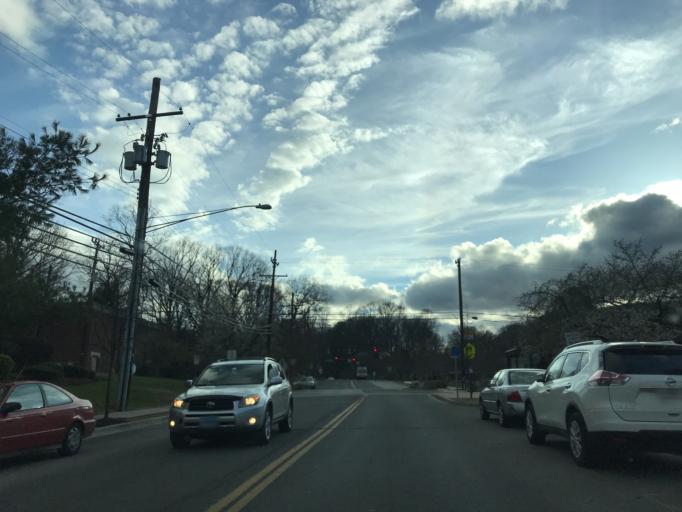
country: US
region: Maryland
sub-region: Montgomery County
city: Takoma Park
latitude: 38.9819
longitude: -77.0089
